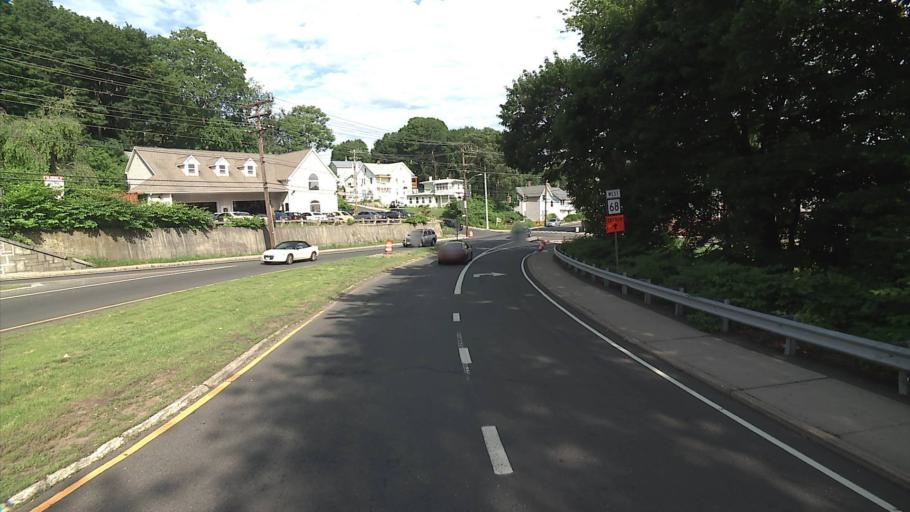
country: US
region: Connecticut
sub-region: New Haven County
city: Naugatuck
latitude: 41.4841
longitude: -73.0560
